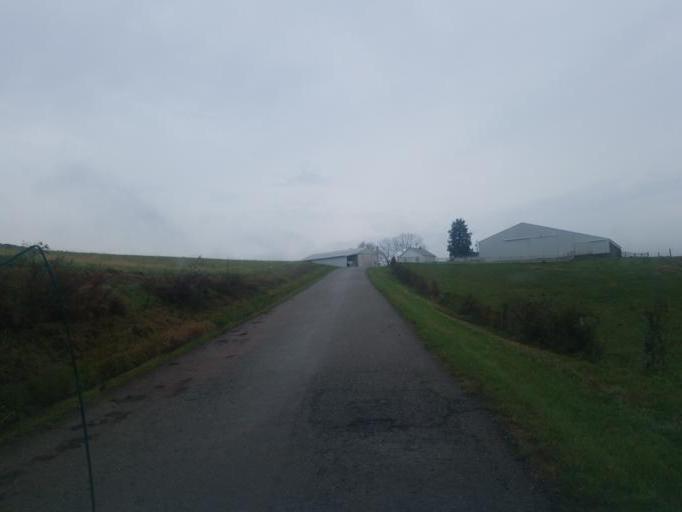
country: US
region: Ohio
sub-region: Morgan County
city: McConnelsville
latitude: 39.5058
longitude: -81.8015
